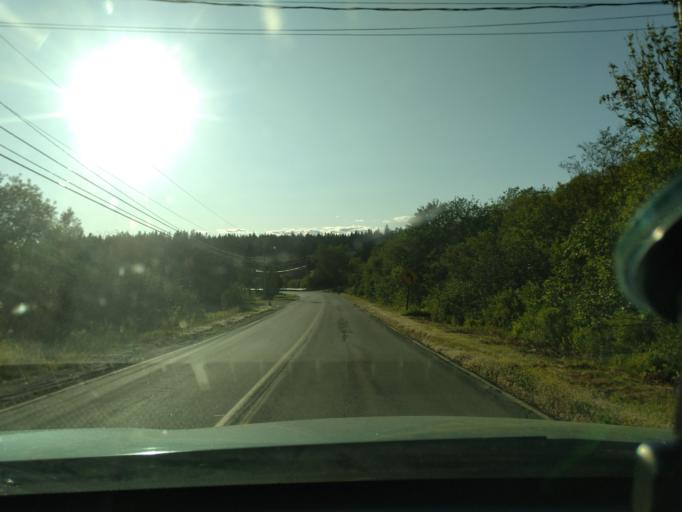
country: US
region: Maine
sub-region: Washington County
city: Machiasport
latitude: 44.6607
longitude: -67.2245
